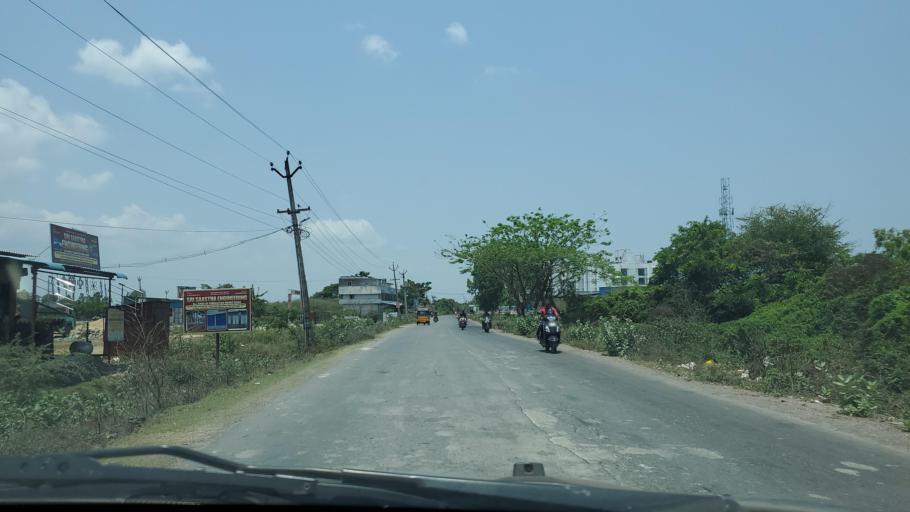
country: IN
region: Tamil Nadu
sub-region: Kancheepuram
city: Vengavasal
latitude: 12.8447
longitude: 80.1701
